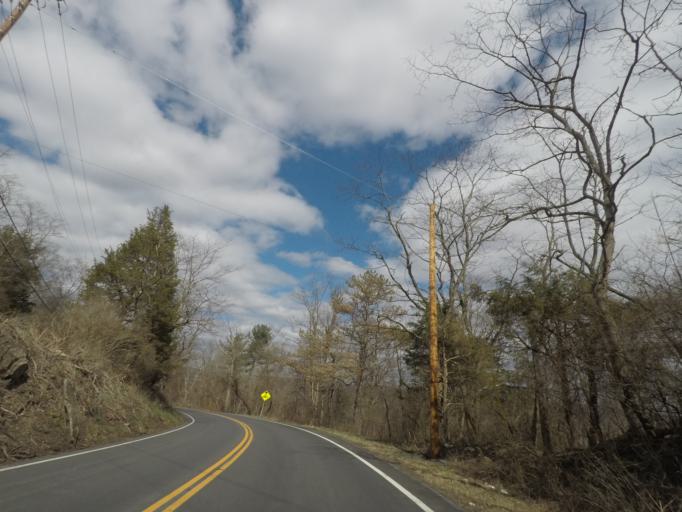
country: US
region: New York
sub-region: Rensselaer County
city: Hampton Manor
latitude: 42.6000
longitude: -73.7732
